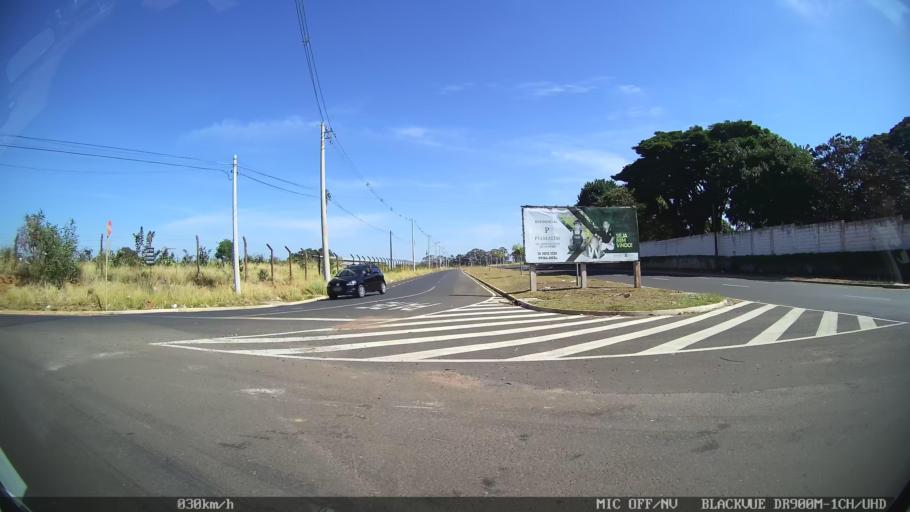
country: BR
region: Sao Paulo
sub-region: Franca
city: Franca
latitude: -20.5434
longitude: -47.4587
